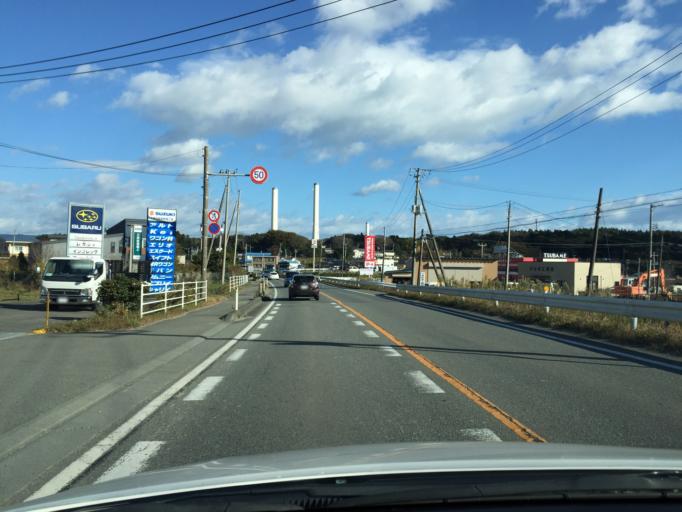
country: JP
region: Fukushima
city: Iwaki
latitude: 37.2183
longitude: 141.0008
